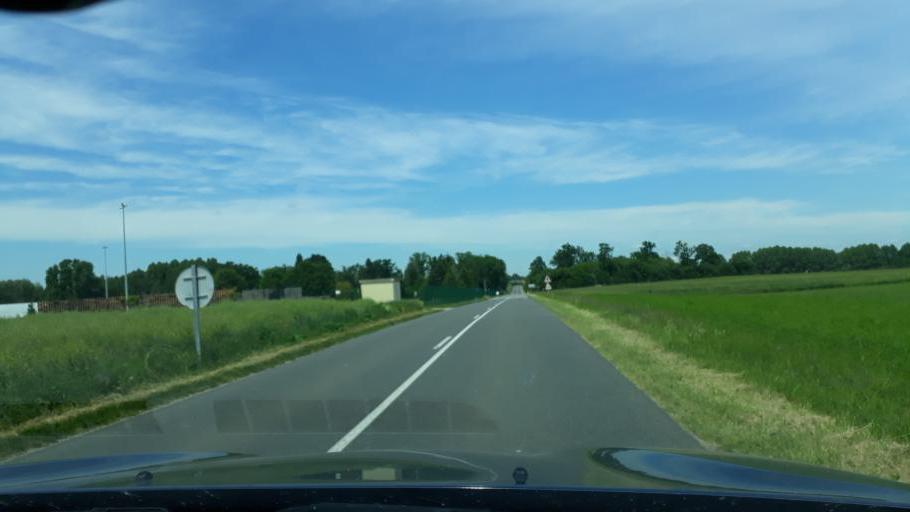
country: FR
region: Centre
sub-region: Departement du Loiret
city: Boiscommun
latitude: 48.0436
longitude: 2.3032
